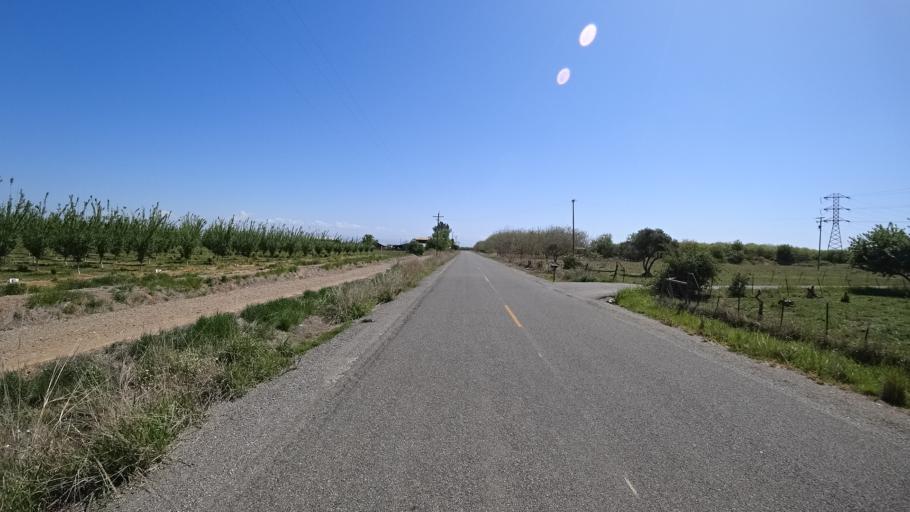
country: US
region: California
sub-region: Glenn County
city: Orland
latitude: 39.7867
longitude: -122.1469
